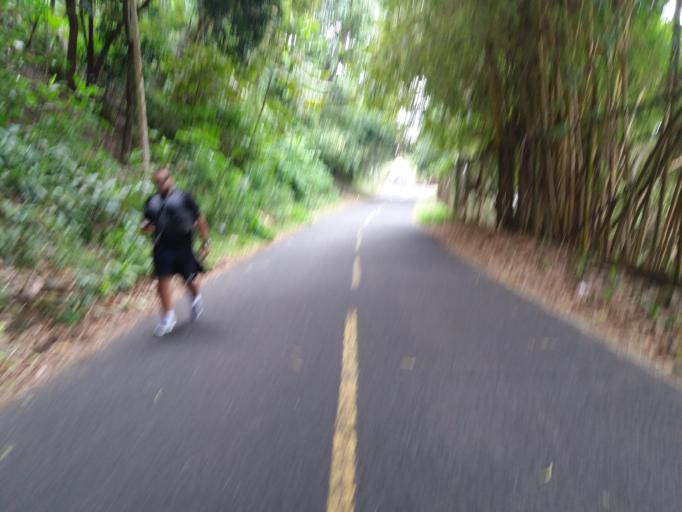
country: PA
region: Panama
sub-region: Distrito de Panama
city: Ancon
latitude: 8.9532
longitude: -79.5489
